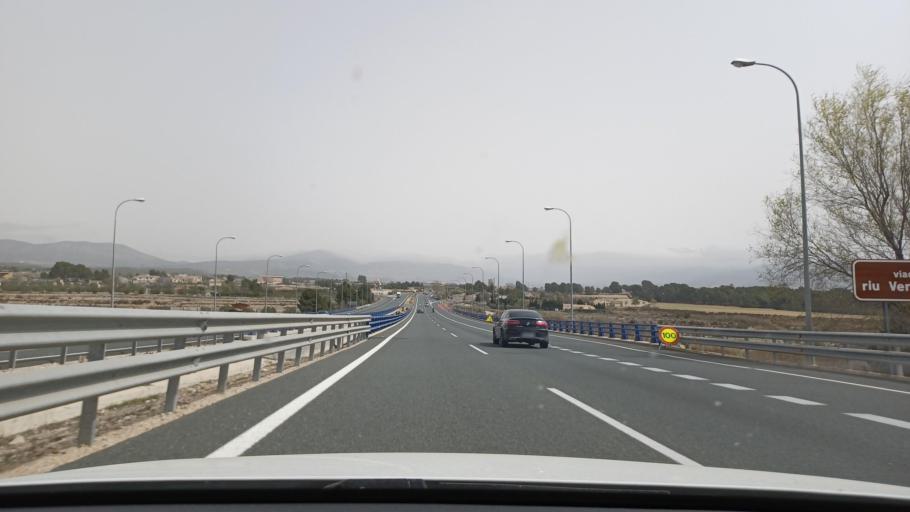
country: ES
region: Valencia
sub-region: Provincia de Alicante
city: Castalla
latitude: 38.5890
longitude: -0.6428
